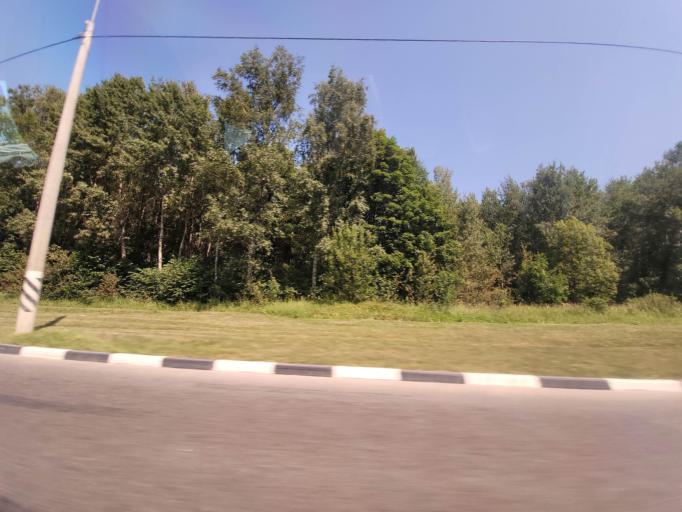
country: RU
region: Kaluga
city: Obninsk
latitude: 55.1253
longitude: 36.6174
